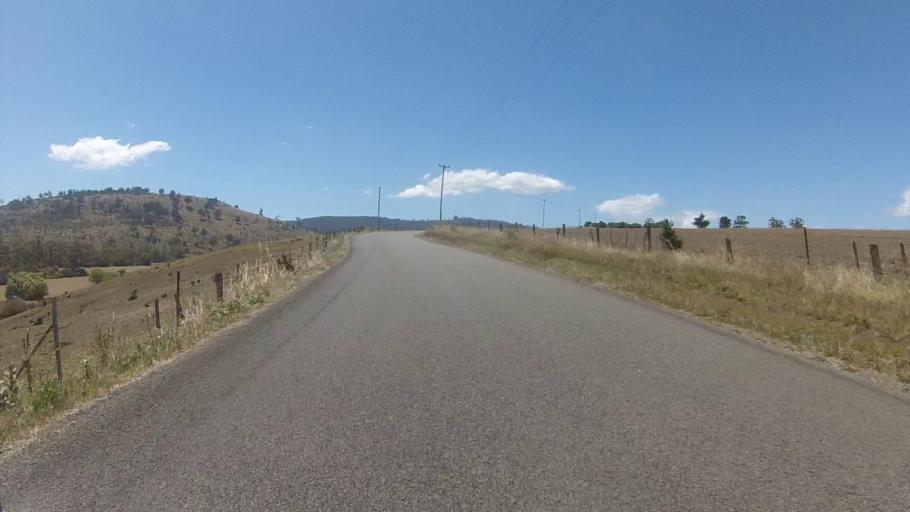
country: AU
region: Tasmania
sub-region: Sorell
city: Sorell
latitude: -42.7696
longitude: 147.5956
